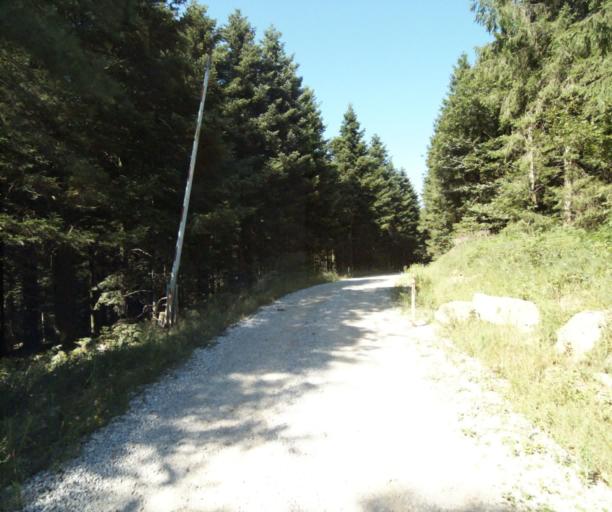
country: FR
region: Midi-Pyrenees
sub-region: Departement du Tarn
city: Soreze
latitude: 43.4357
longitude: 2.1092
